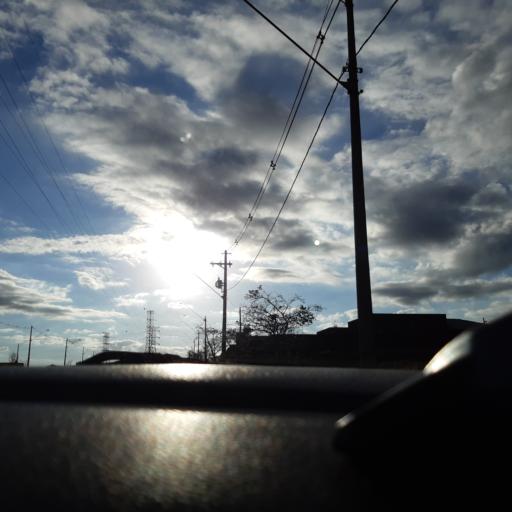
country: BR
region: Sao Paulo
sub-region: Ourinhos
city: Ourinhos
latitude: -22.9981
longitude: -49.8500
